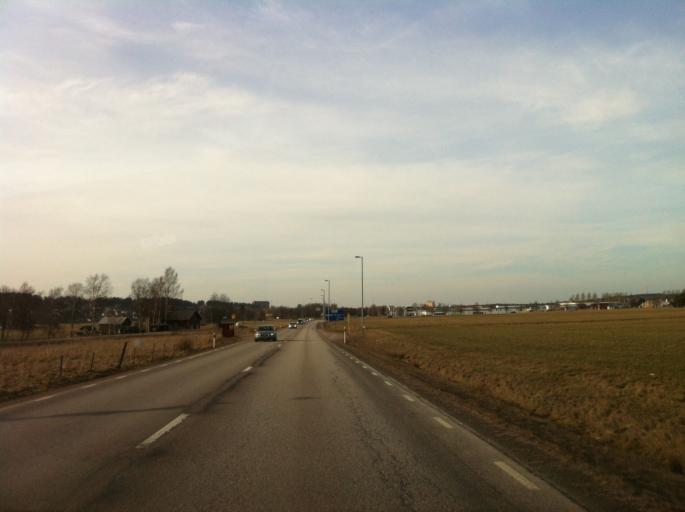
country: SE
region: Vaermland
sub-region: Kristinehamns Kommun
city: Kristinehamn
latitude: 59.2914
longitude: 14.1314
